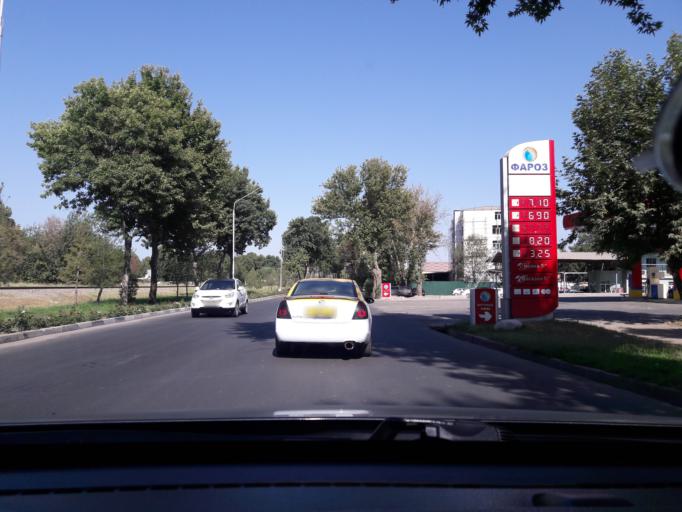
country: TJ
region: Dushanbe
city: Dushanbe
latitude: 38.5694
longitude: 68.7610
